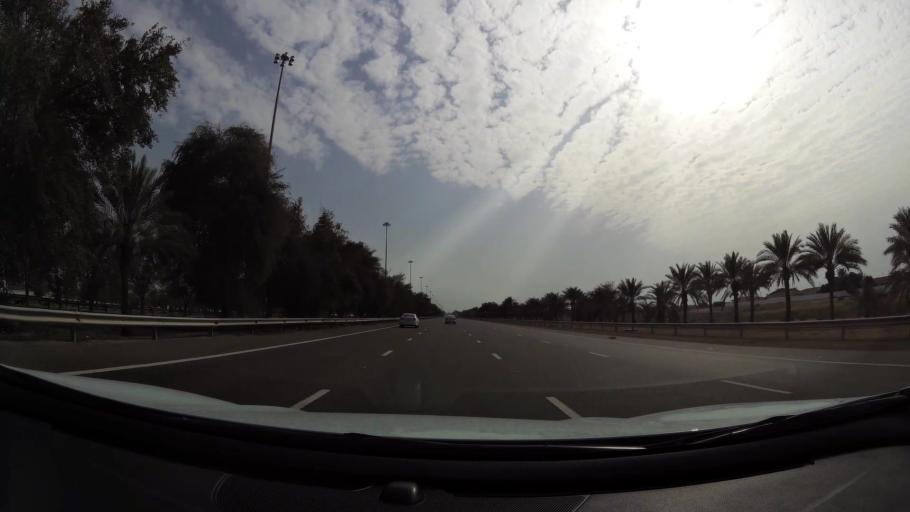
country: AE
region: Abu Dhabi
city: Abu Dhabi
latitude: 24.5171
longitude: 54.6888
